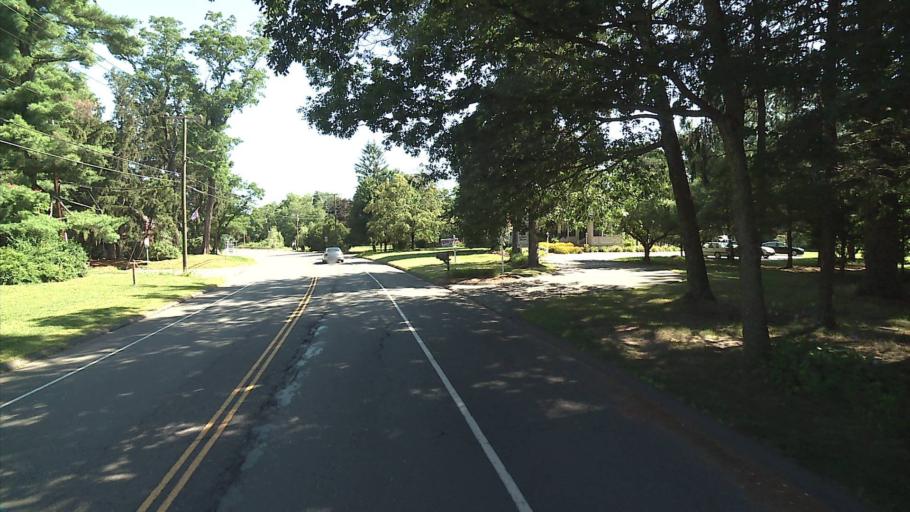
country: US
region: Connecticut
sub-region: Hartford County
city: Weatogue
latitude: 41.8437
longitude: -72.8116
